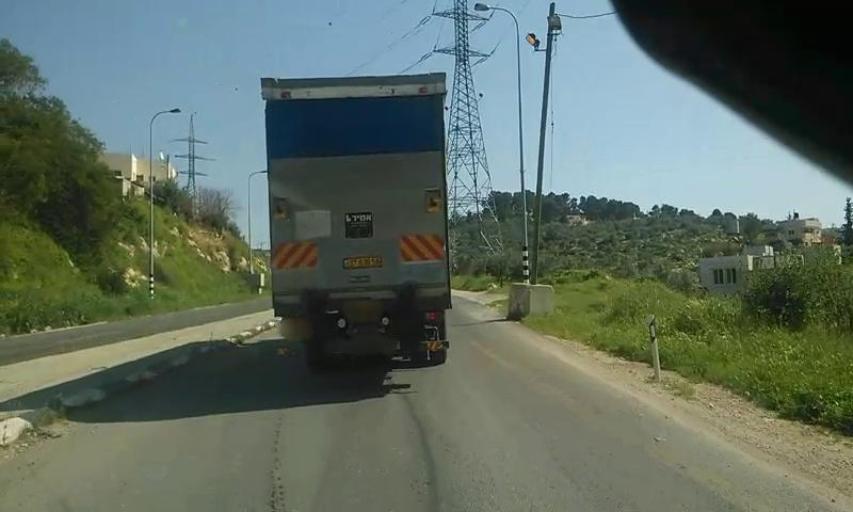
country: PS
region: West Bank
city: Idhna
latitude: 31.5702
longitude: 34.9853
